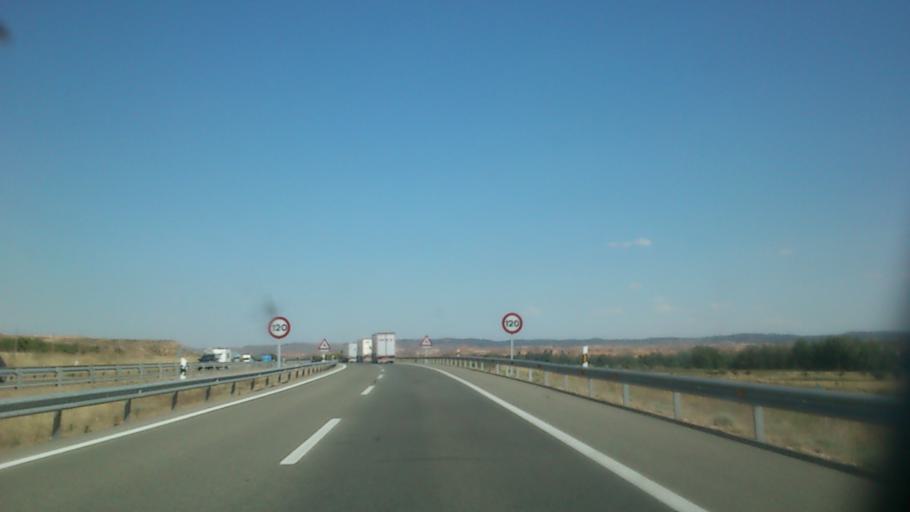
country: ES
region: Aragon
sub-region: Provincia de Zaragoza
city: Cetina
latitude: 41.3084
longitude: -1.9923
